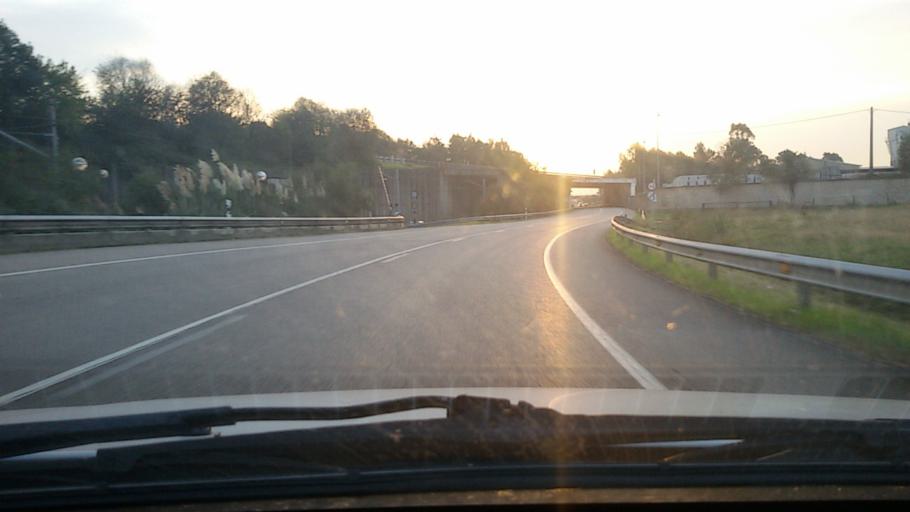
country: ES
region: Asturias
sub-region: Province of Asturias
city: Norena
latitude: 43.3819
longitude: -5.7295
